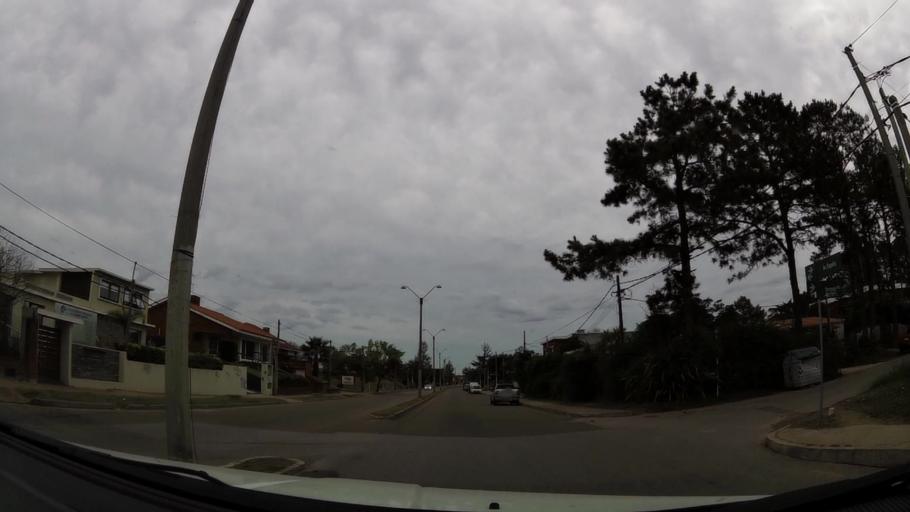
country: UY
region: Maldonado
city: Maldonado
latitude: -34.9153
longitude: -54.9688
